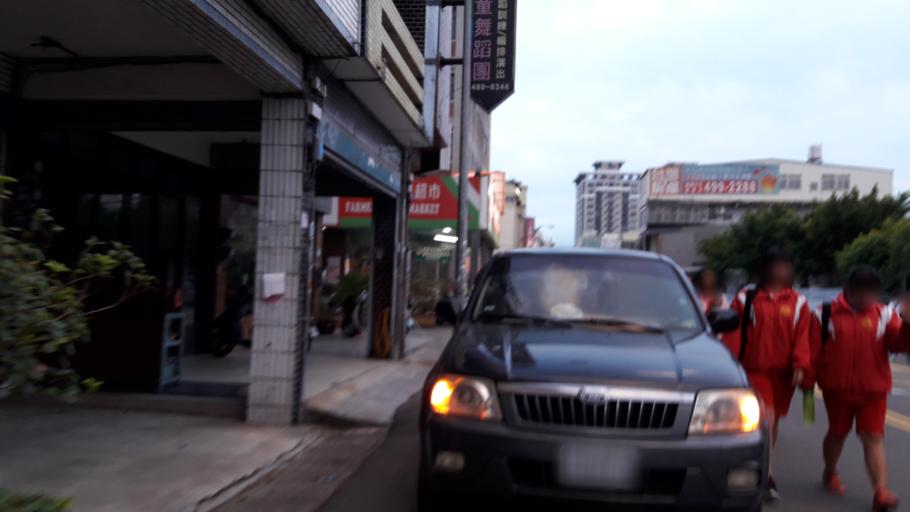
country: TW
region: Taiwan
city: Daxi
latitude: 24.8625
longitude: 121.2152
